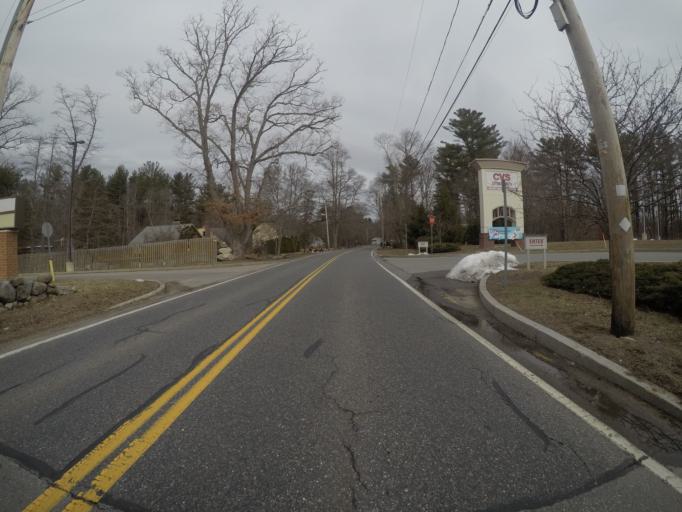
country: US
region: Massachusetts
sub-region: Bristol County
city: Easton
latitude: 42.0249
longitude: -71.1199
